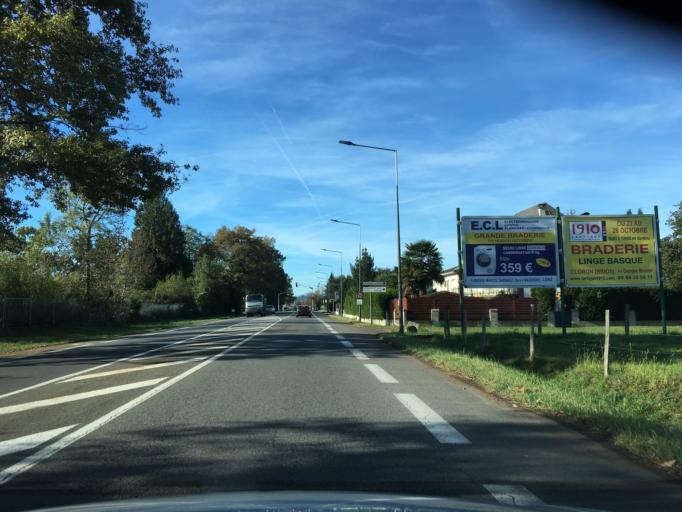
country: FR
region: Aquitaine
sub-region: Departement des Pyrenees-Atlantiques
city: Idron
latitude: 43.3123
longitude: -0.3215
